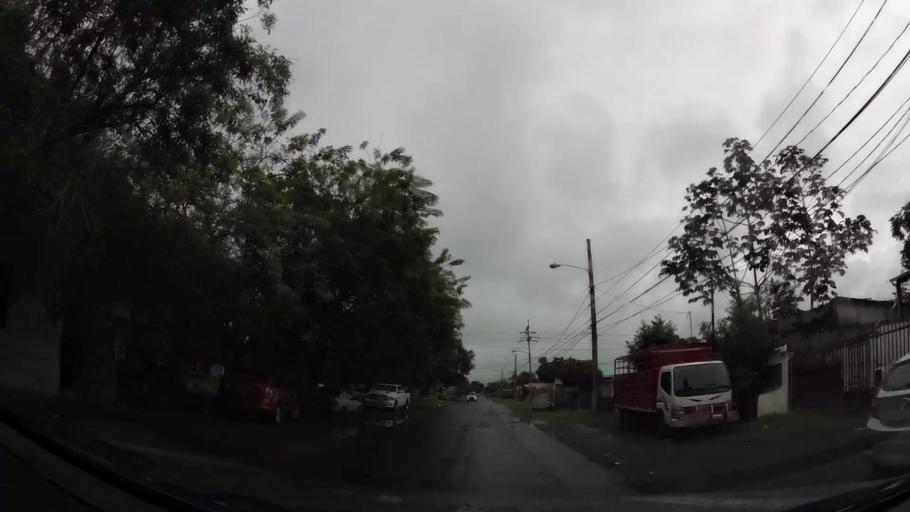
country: PA
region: Chiriqui
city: David
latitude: 8.4295
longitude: -82.4326
